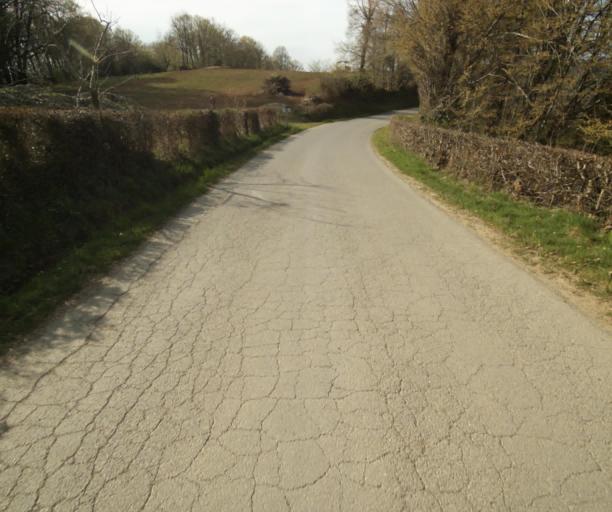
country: FR
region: Limousin
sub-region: Departement de la Correze
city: Naves
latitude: 45.3078
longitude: 1.7338
